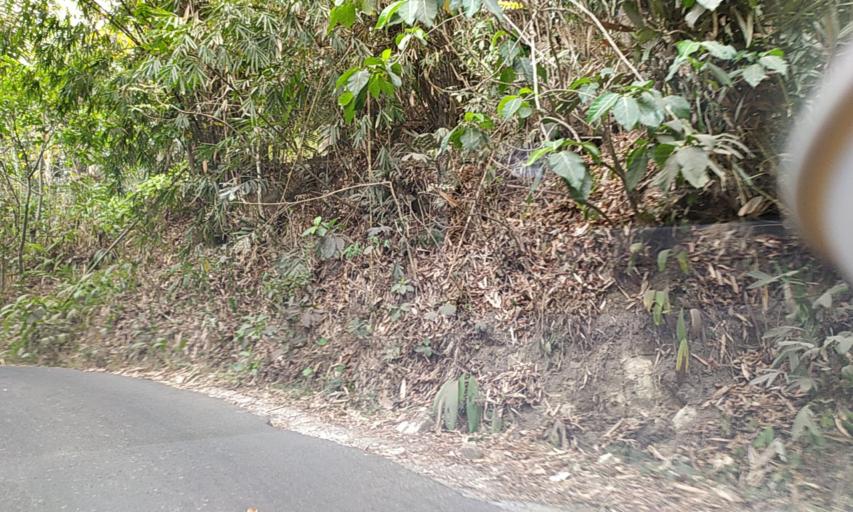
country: ID
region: Central Java
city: Telagasari
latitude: -7.3011
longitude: 108.8159
